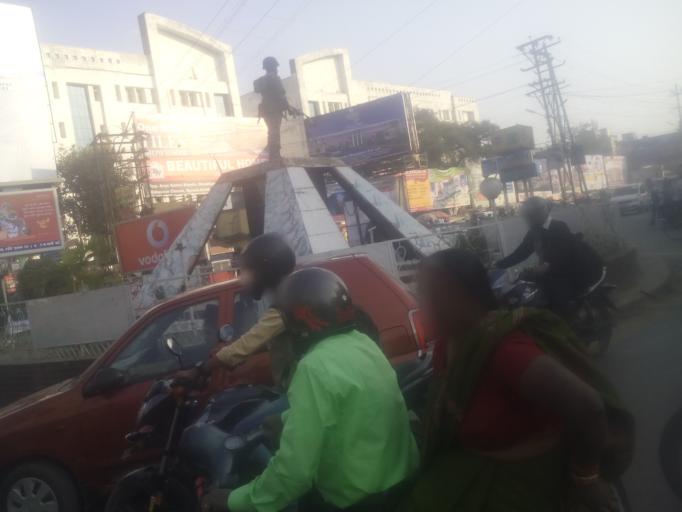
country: IN
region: Jharkhand
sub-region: Ranchi
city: Ranchi
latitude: 23.3702
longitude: 85.3249
